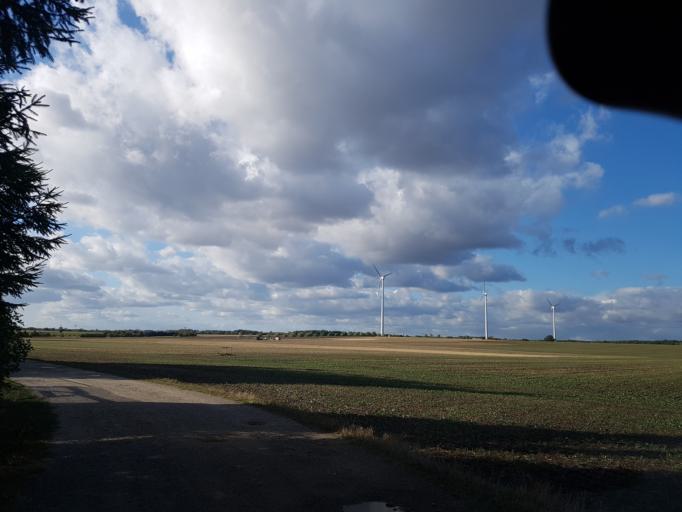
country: DE
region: Brandenburg
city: Doberlug-Kirchhain
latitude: 51.6120
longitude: 13.5966
